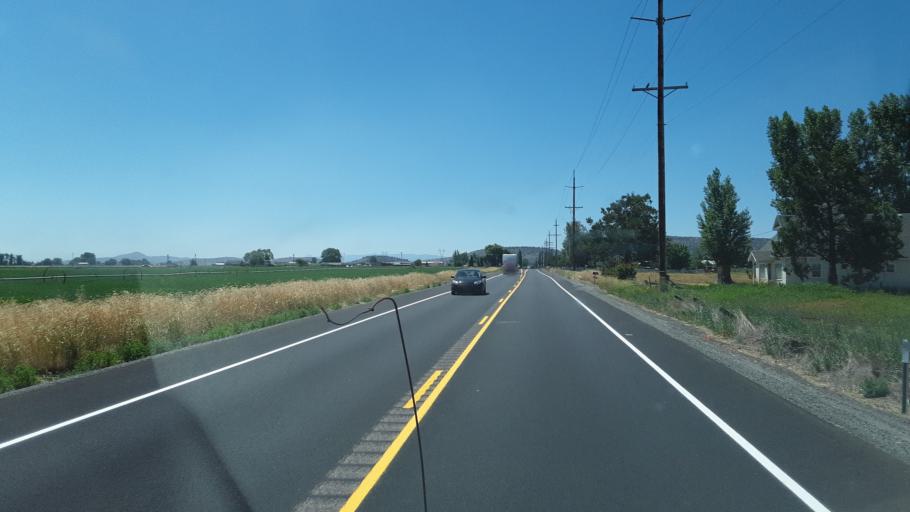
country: US
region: Oregon
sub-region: Klamath County
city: Altamont
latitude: 42.1165
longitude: -121.6985
